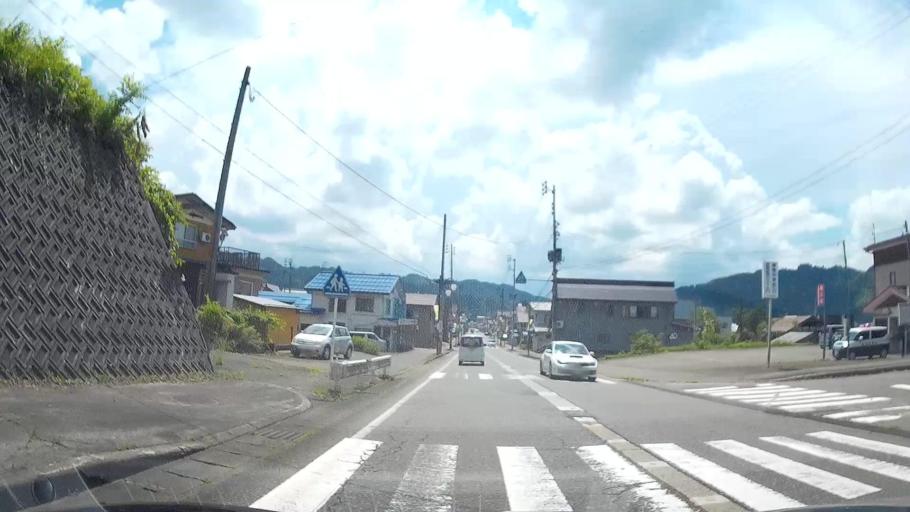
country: JP
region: Niigata
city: Tokamachi
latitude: 37.0170
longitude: 138.6547
